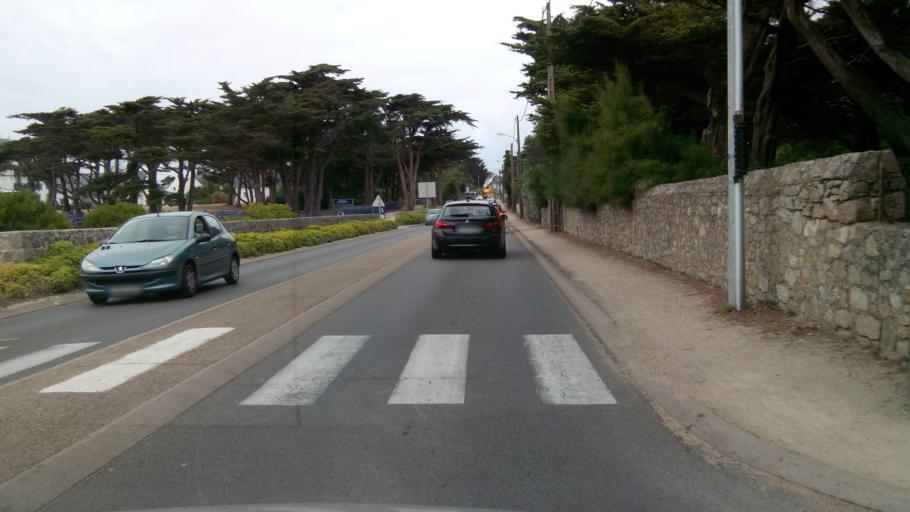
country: FR
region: Pays de la Loire
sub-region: Departement de la Loire-Atlantique
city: Batz-sur-Mer
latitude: 47.2815
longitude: -2.4974
